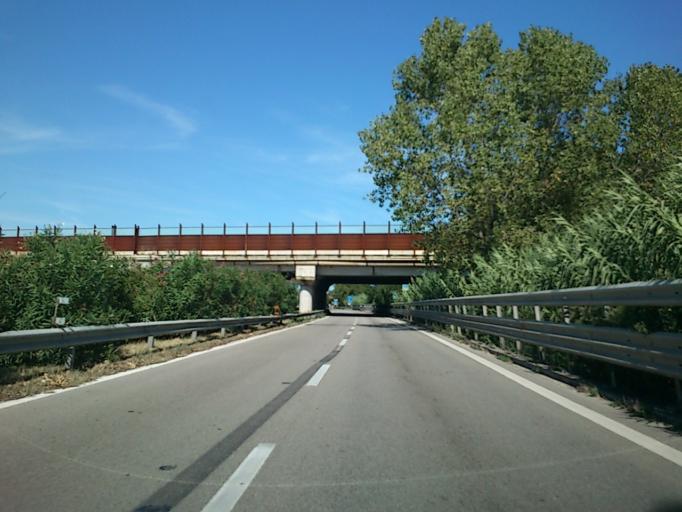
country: IT
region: The Marches
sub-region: Provincia di Pesaro e Urbino
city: Rosciano
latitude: 43.8133
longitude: 13.0179
